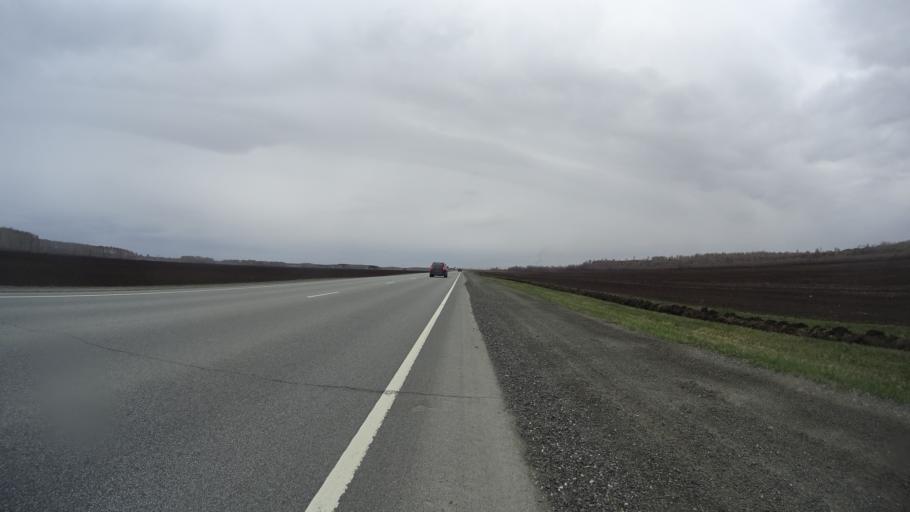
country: RU
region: Chelyabinsk
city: Krasnogorskiy
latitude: 54.5736
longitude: 61.2910
